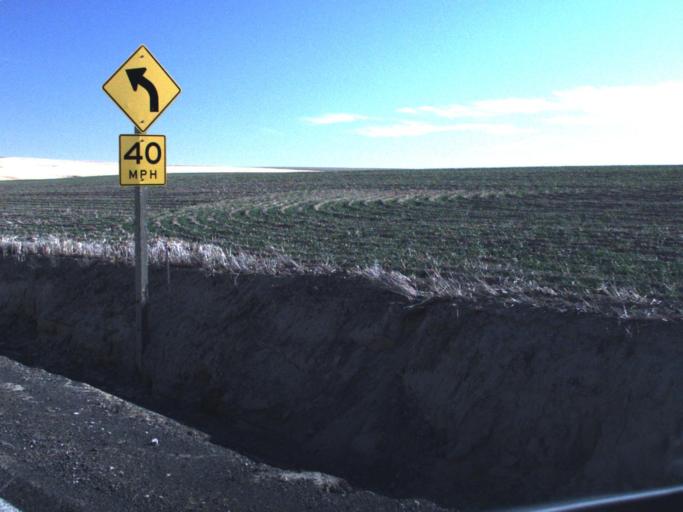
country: US
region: Washington
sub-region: Adams County
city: Ritzville
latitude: 47.1661
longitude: -118.6856
